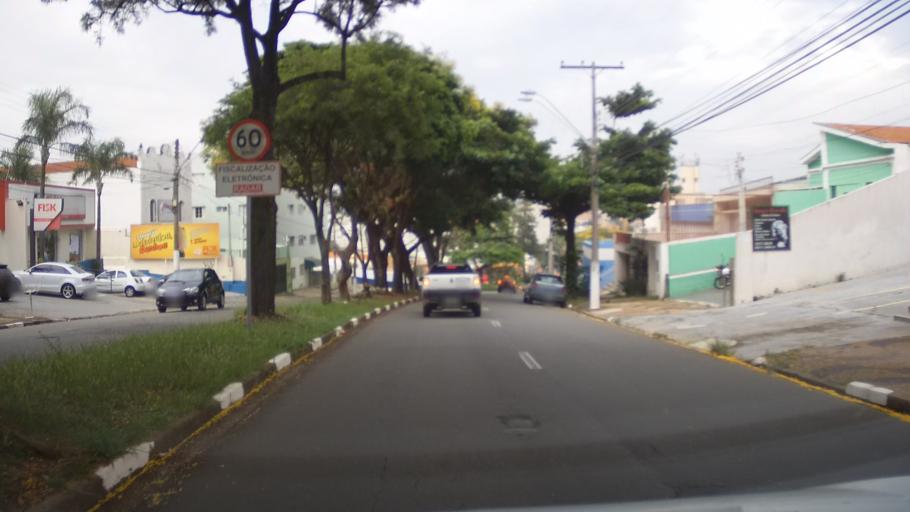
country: BR
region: Sao Paulo
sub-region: Campinas
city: Campinas
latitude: -22.9240
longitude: -47.0555
